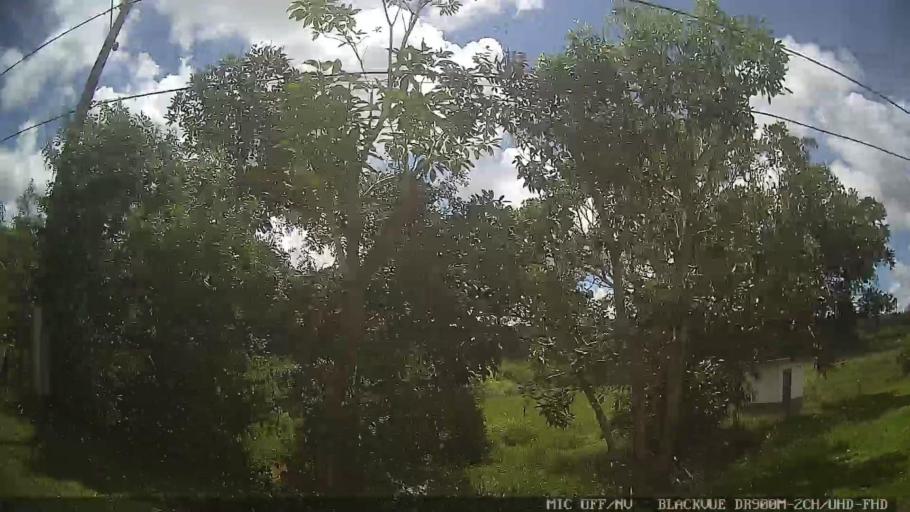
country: BR
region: Sao Paulo
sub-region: Amparo
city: Amparo
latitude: -22.8086
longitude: -46.6976
